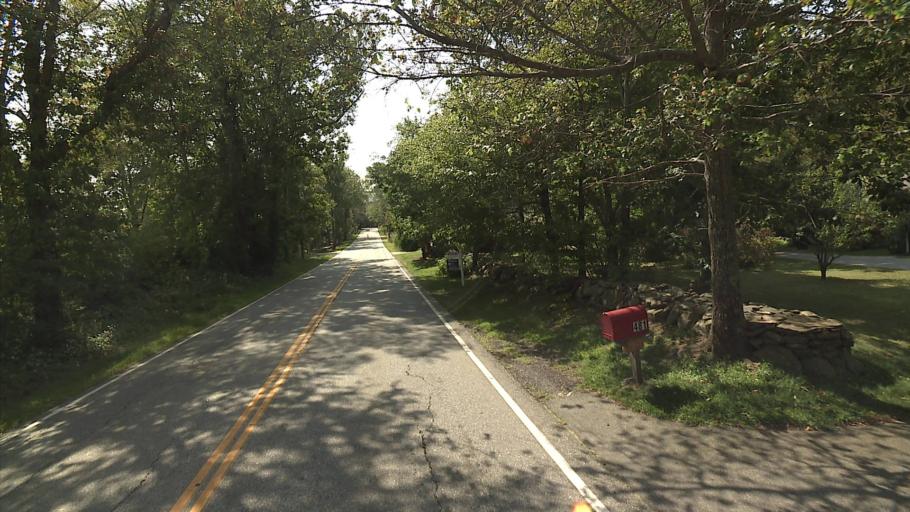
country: US
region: Connecticut
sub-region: Windham County
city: East Brooklyn
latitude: 41.8205
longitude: -71.9582
